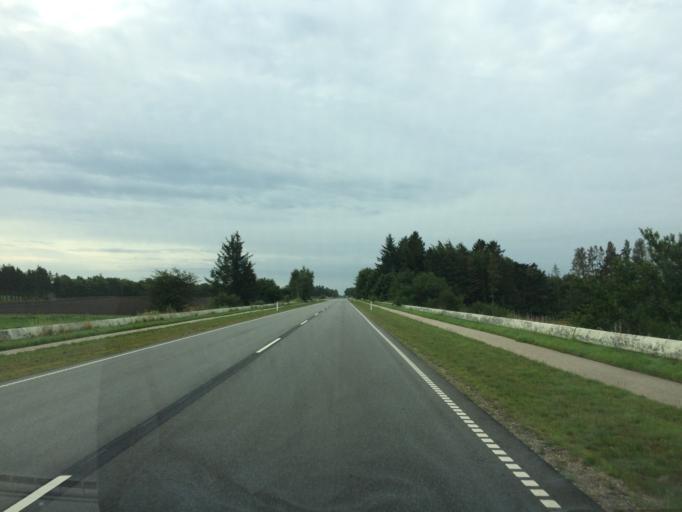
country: DK
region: Central Jutland
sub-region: Herning Kommune
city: Lind
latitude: 56.0745
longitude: 8.9867
